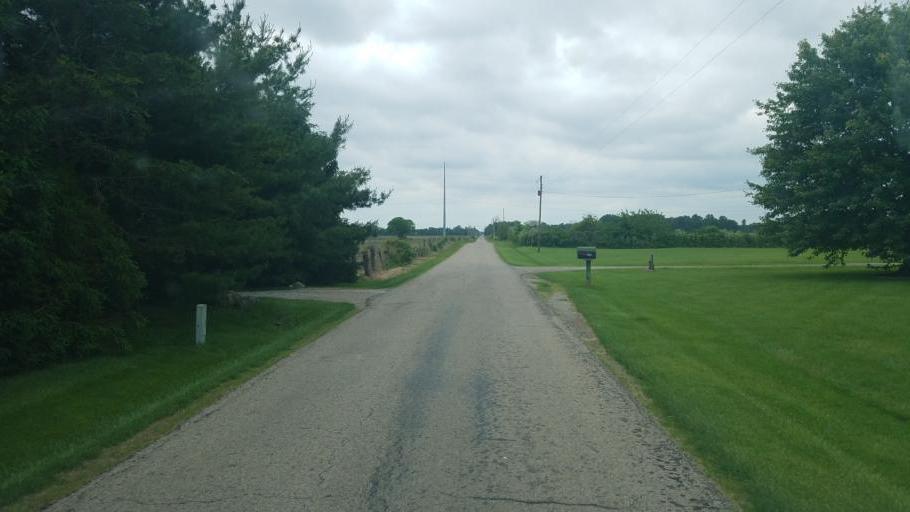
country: US
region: Ohio
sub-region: Fairfield County
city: Millersport
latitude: 39.9343
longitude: -82.5816
